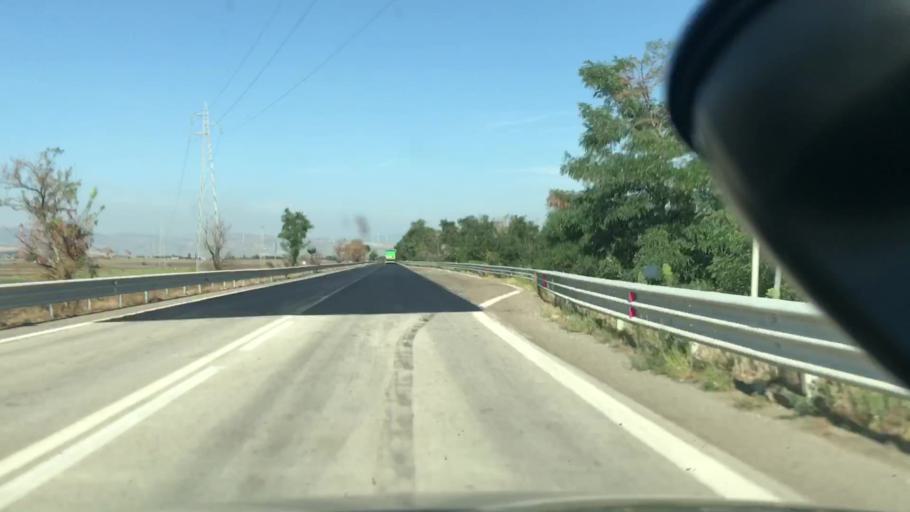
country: IT
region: Basilicate
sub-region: Provincia di Potenza
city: Zona 179
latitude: 41.0768
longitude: 15.6395
